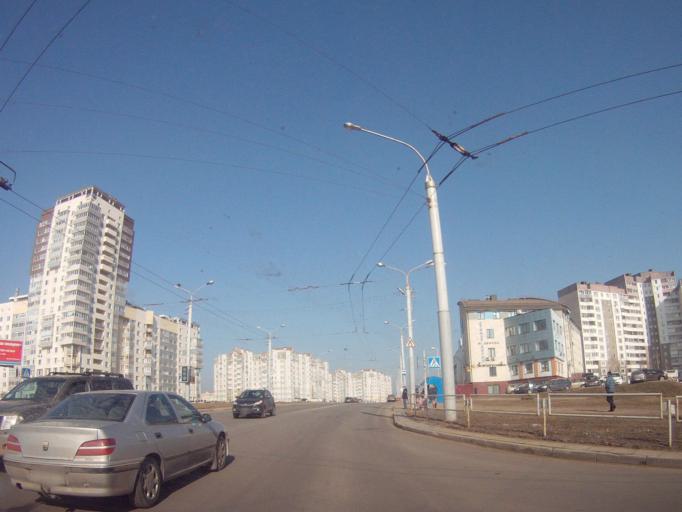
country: BY
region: Minsk
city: Novoye Medvezhino
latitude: 53.8882
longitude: 27.4289
